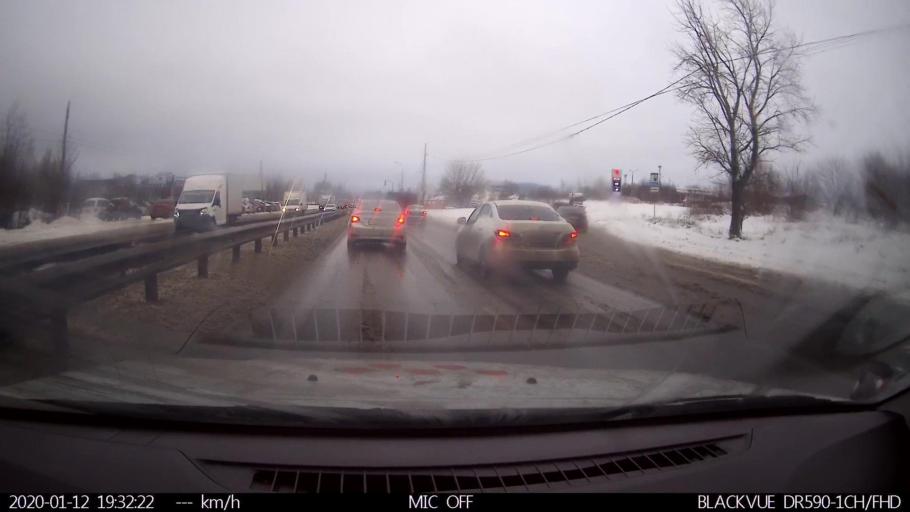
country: RU
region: Nizjnij Novgorod
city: Nizhniy Novgorod
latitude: 56.2417
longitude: 43.9902
